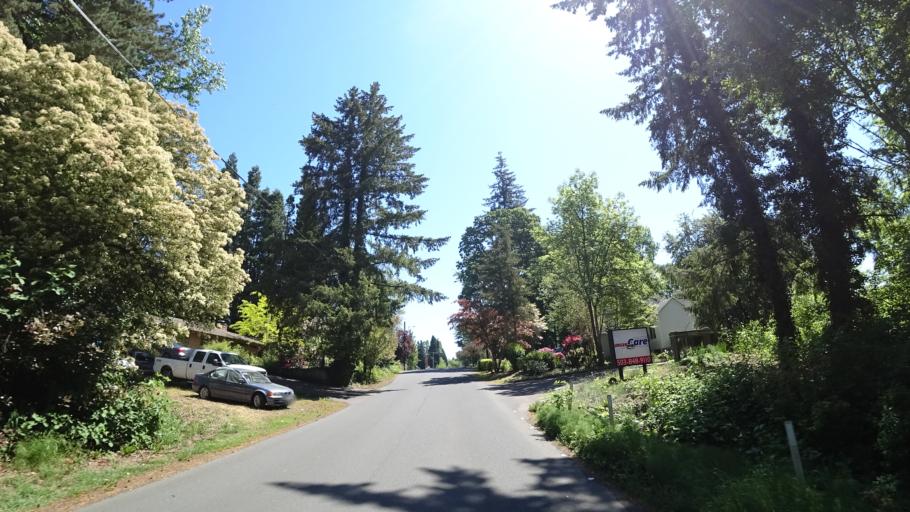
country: US
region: Oregon
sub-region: Washington County
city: Aloha
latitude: 45.4942
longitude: -122.8583
